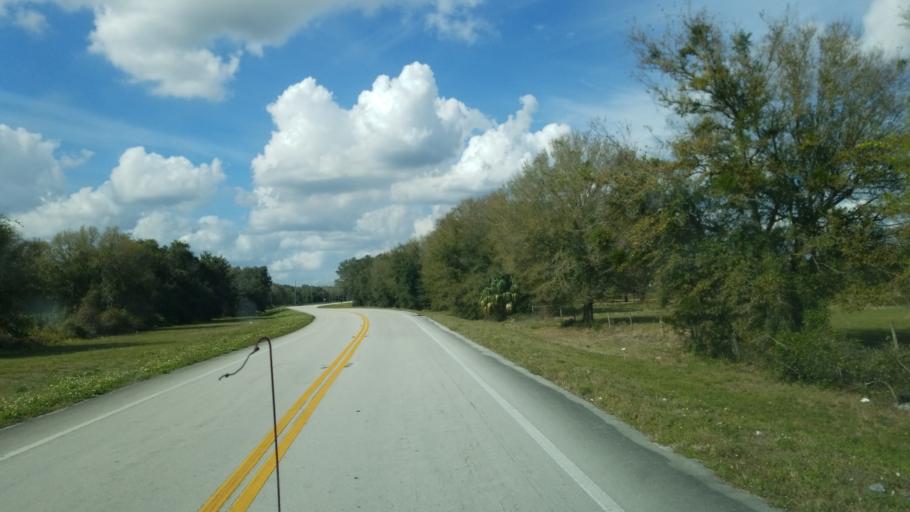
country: US
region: Florida
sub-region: Osceola County
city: Saint Cloud
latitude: 28.0212
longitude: -81.0338
